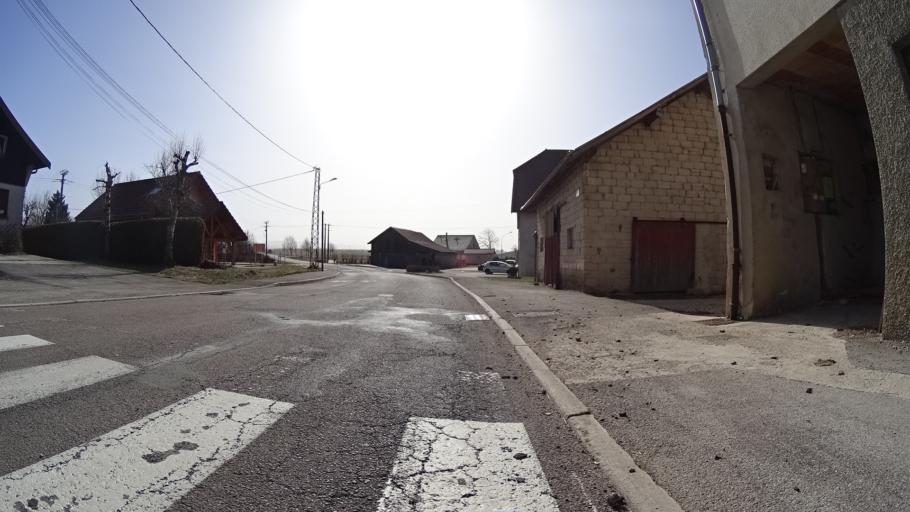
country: FR
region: Franche-Comte
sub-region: Departement du Doubs
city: Frasne
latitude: 46.8516
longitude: 6.1543
